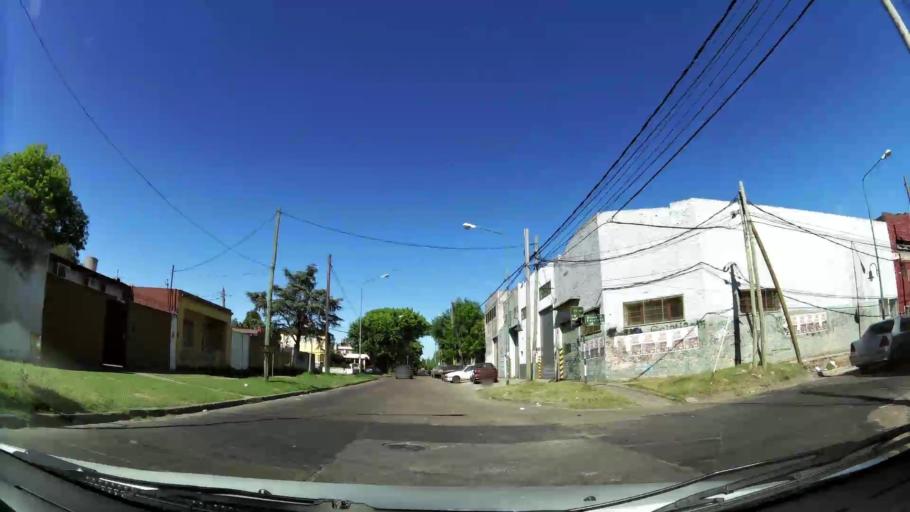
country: AR
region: Buenos Aires
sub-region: Partido de General San Martin
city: General San Martin
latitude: -34.5457
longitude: -58.5218
